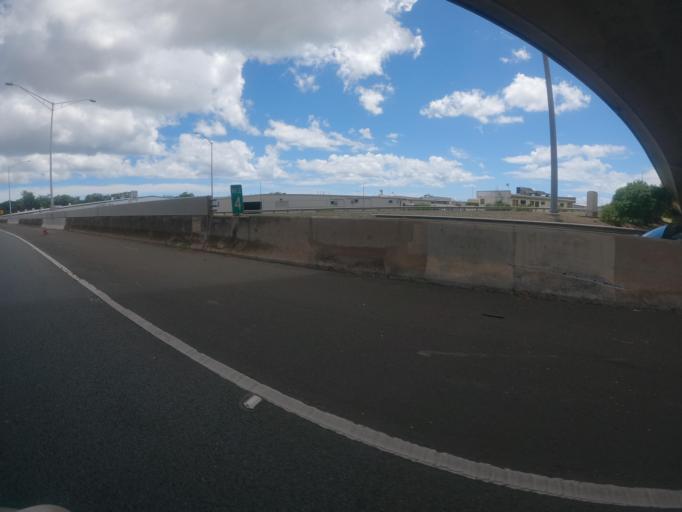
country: US
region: Hawaii
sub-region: Honolulu County
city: Halawa Heights
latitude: 21.3442
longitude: -157.8926
